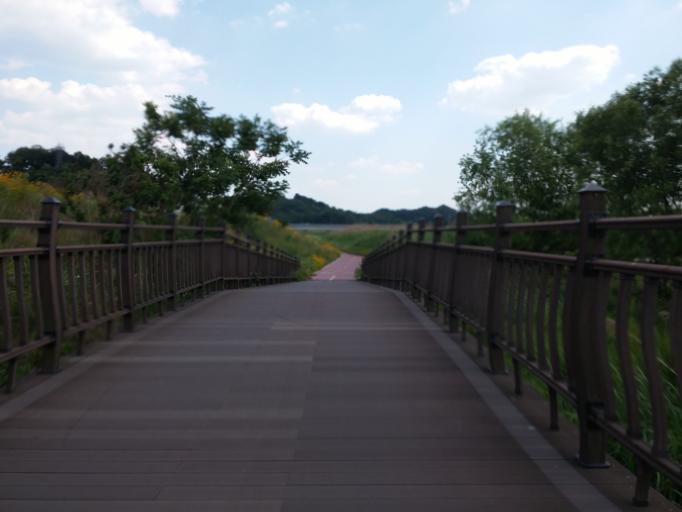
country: KR
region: Chungcheongbuk-do
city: Cheongju-si
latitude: 36.5680
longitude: 127.5076
